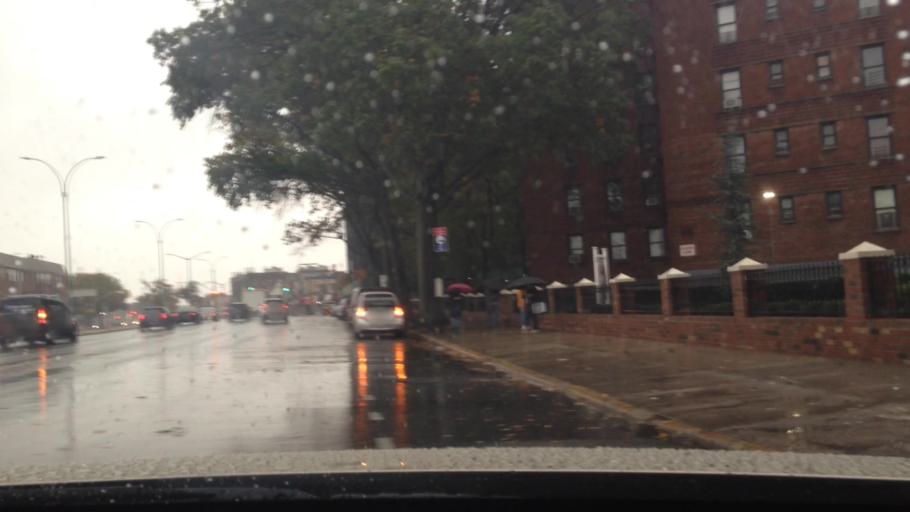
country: US
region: New York
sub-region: Queens County
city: Borough of Queens
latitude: 40.7259
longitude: -73.8703
